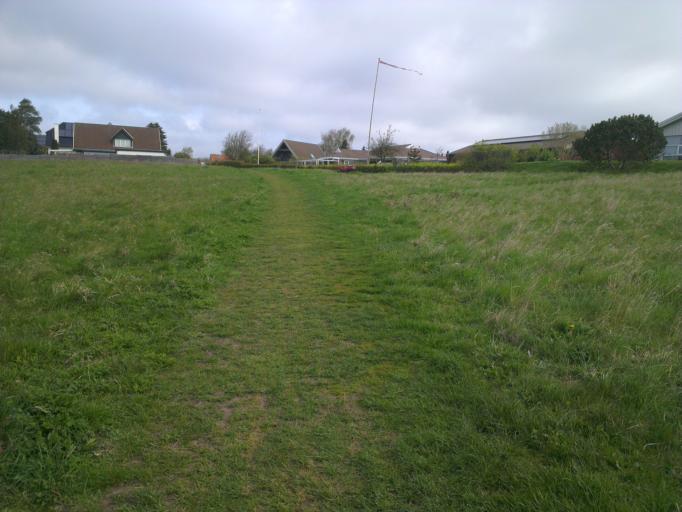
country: DK
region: Capital Region
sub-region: Frederikssund Kommune
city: Frederikssund
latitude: 55.8216
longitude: 12.0658
